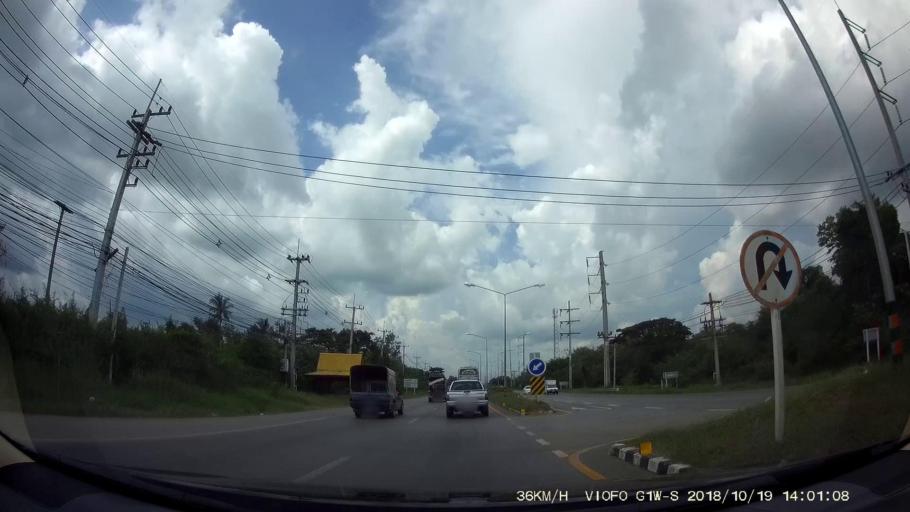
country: TH
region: Chaiyaphum
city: Chaiyaphum
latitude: 15.8266
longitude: 102.0590
